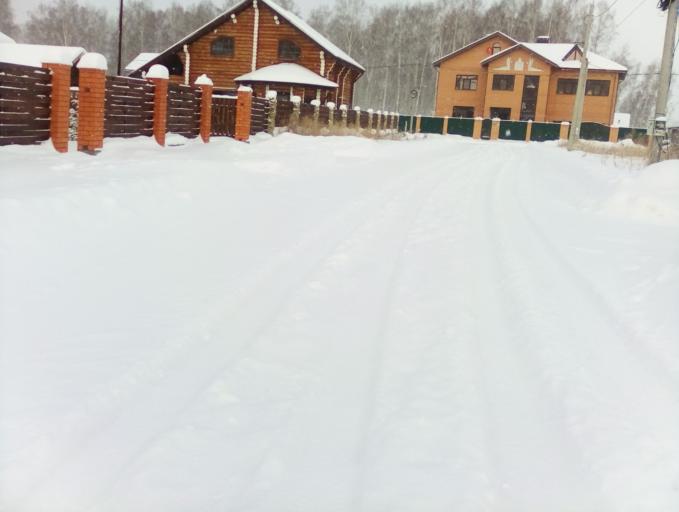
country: RU
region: Chelyabinsk
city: Poletayevo
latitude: 55.1547
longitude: 61.1400
